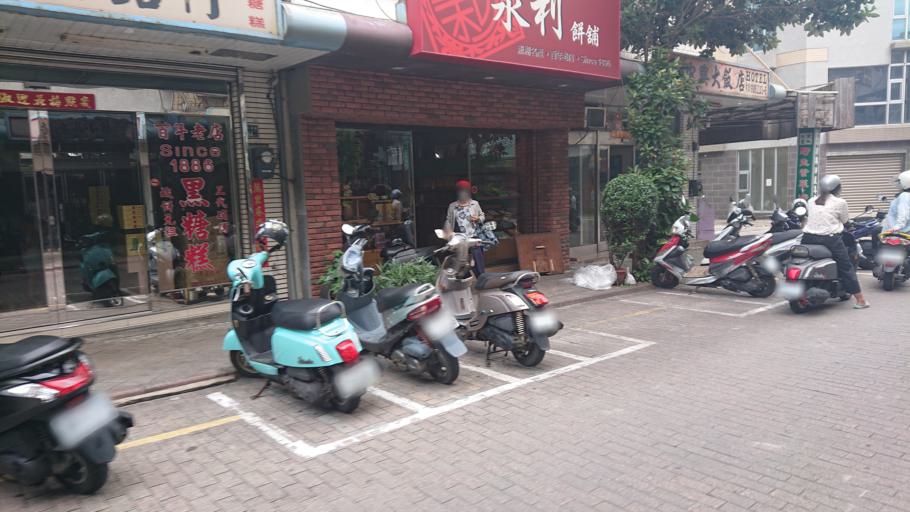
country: TW
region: Taiwan
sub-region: Penghu
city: Ma-kung
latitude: 23.5668
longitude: 119.5678
